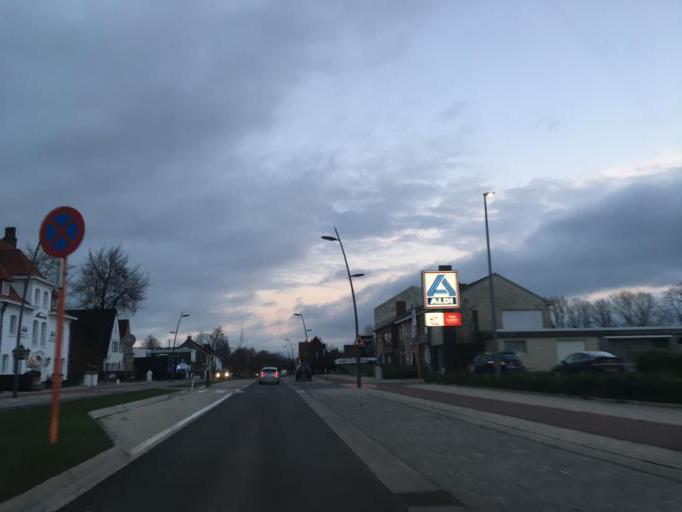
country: BE
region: Flanders
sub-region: Provincie West-Vlaanderen
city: Roeselare
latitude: 50.9501
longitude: 3.1121
